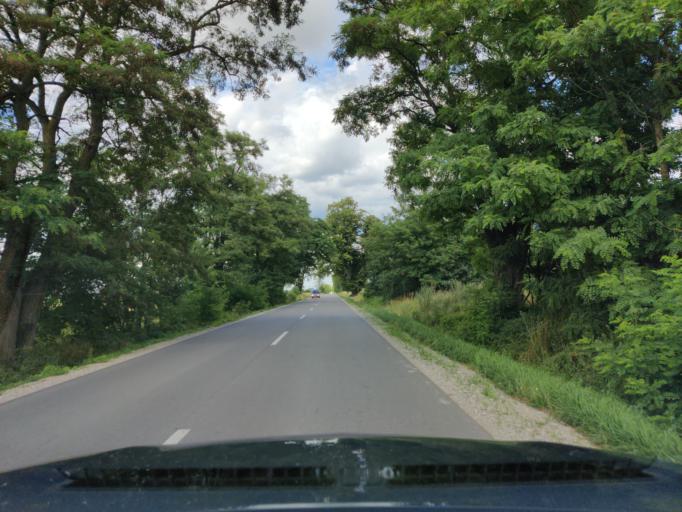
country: PL
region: Masovian Voivodeship
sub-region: Powiat sokolowski
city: Kosow Lacki
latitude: 52.5540
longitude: 22.1070
